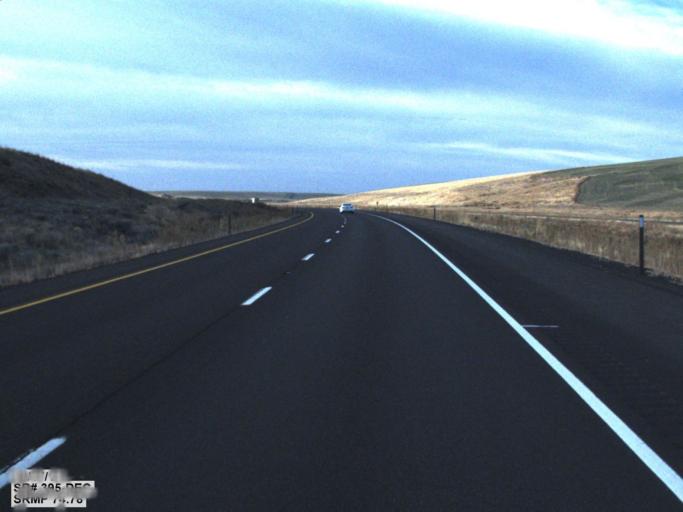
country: US
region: Washington
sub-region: Franklin County
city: Connell
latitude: 46.8730
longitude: -118.6293
